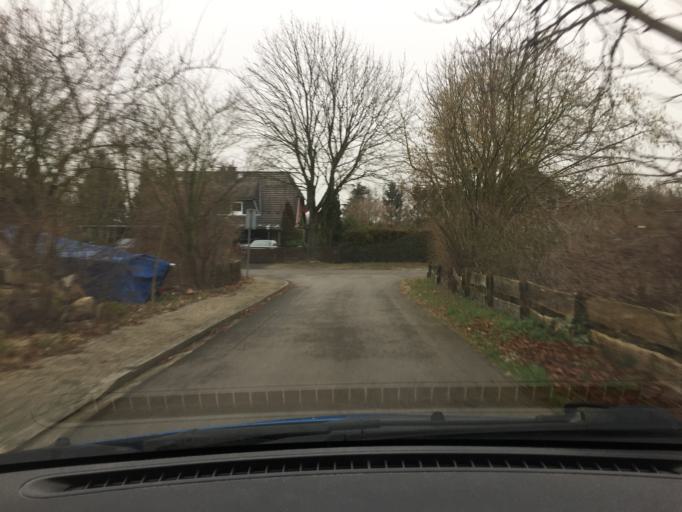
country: DE
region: Lower Saxony
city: Kirchgellersen
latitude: 53.2321
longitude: 10.2871
